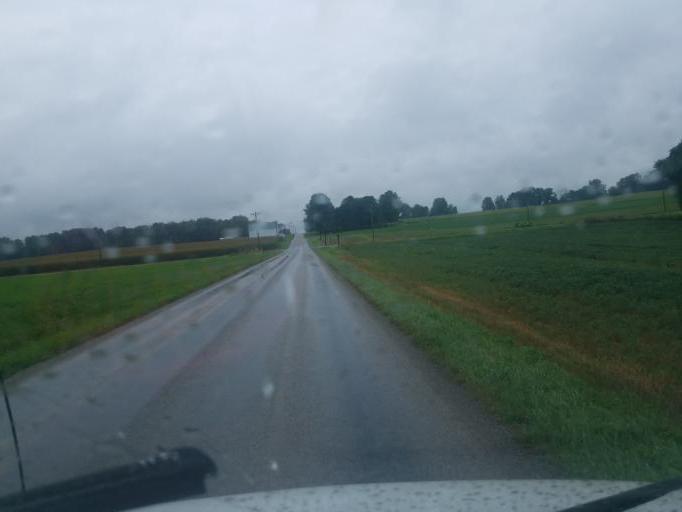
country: US
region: Ohio
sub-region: Wayne County
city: Creston
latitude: 40.9743
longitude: -81.9367
